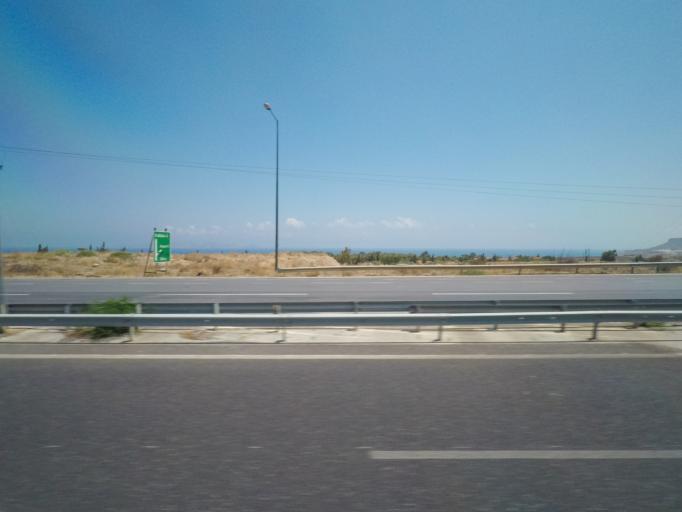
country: GR
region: Crete
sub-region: Nomos Irakleiou
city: Nea Alikarnassos
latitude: 35.3285
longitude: 25.1761
